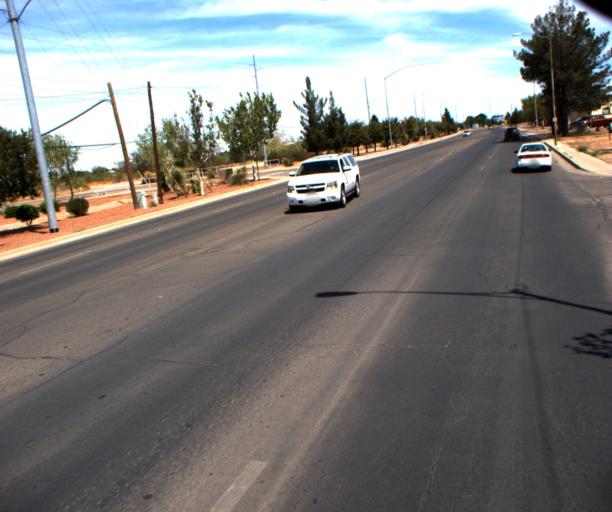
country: US
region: Arizona
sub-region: Cochise County
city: Douglas
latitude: 31.3454
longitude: -109.5566
